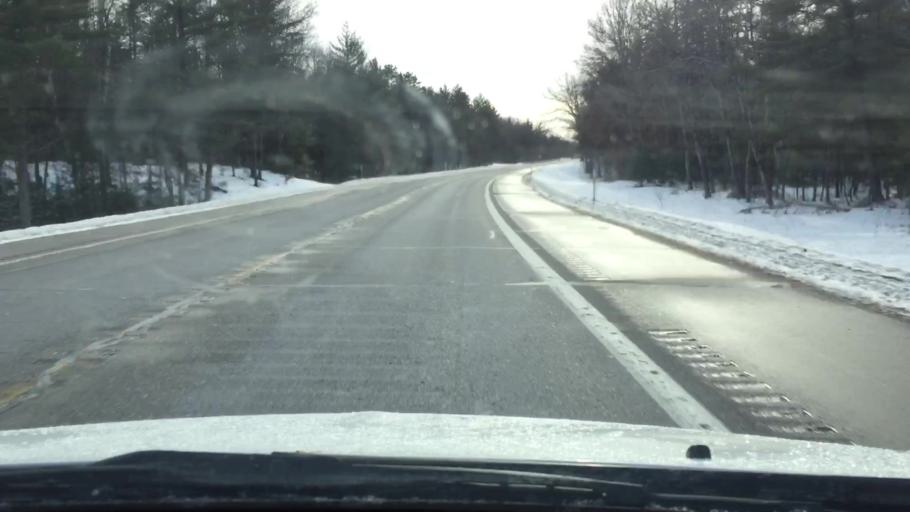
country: US
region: Michigan
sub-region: Wexford County
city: Manton
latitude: 44.5453
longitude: -85.3713
